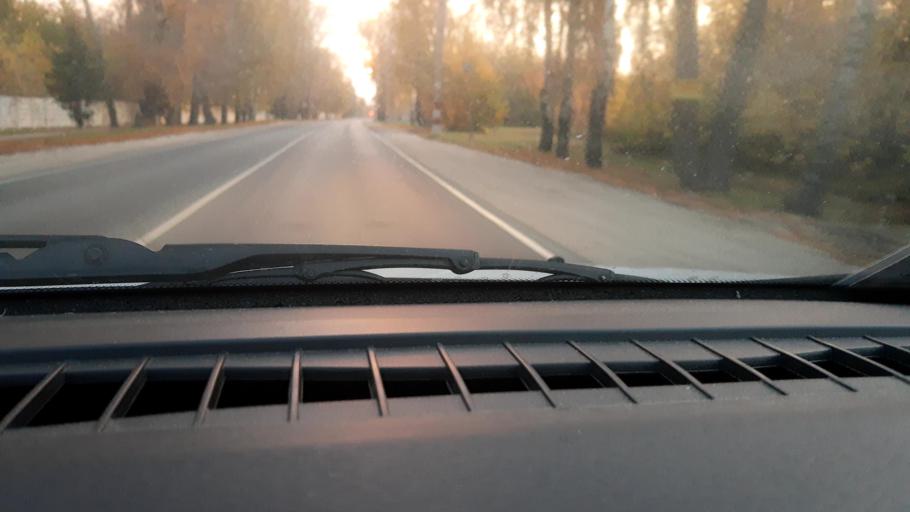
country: RU
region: Nizjnij Novgorod
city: Bor
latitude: 56.3793
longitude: 44.0326
